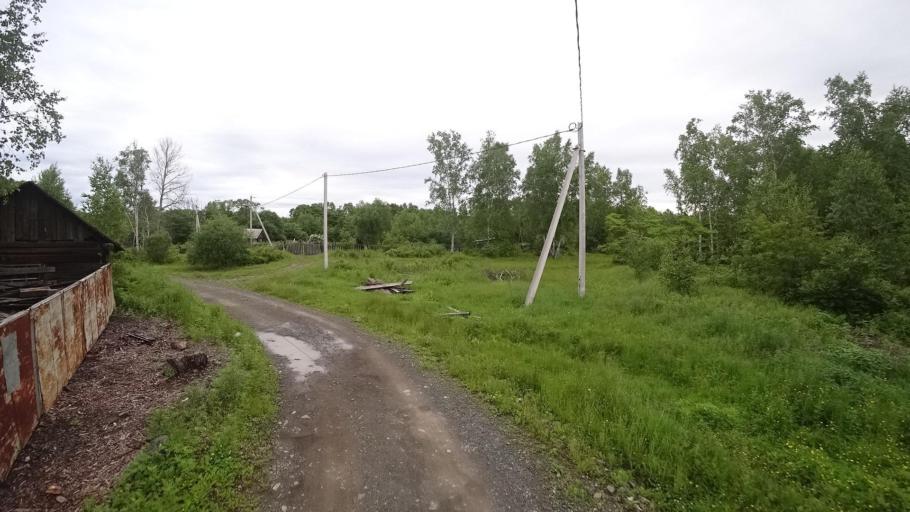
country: RU
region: Khabarovsk Krai
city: Amursk
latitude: 49.9041
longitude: 136.1357
